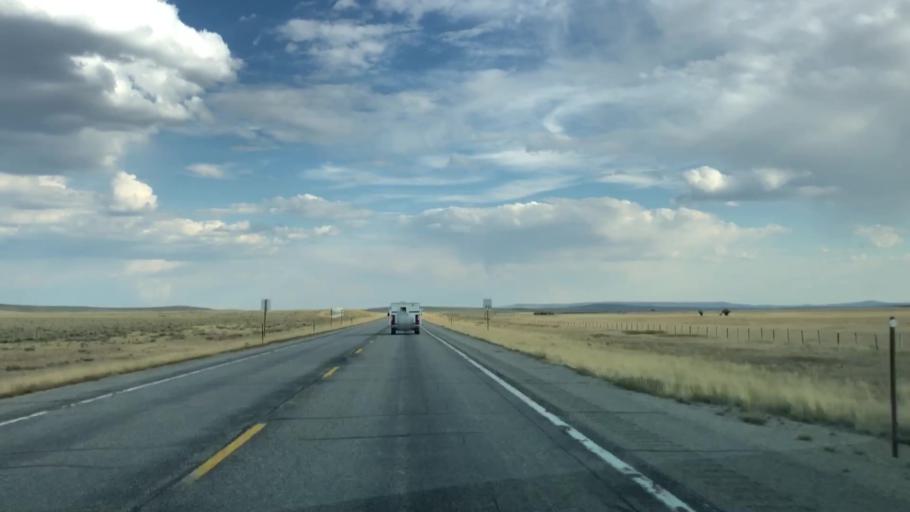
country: US
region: Wyoming
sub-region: Sublette County
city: Pinedale
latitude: 43.0414
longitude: -110.1403
